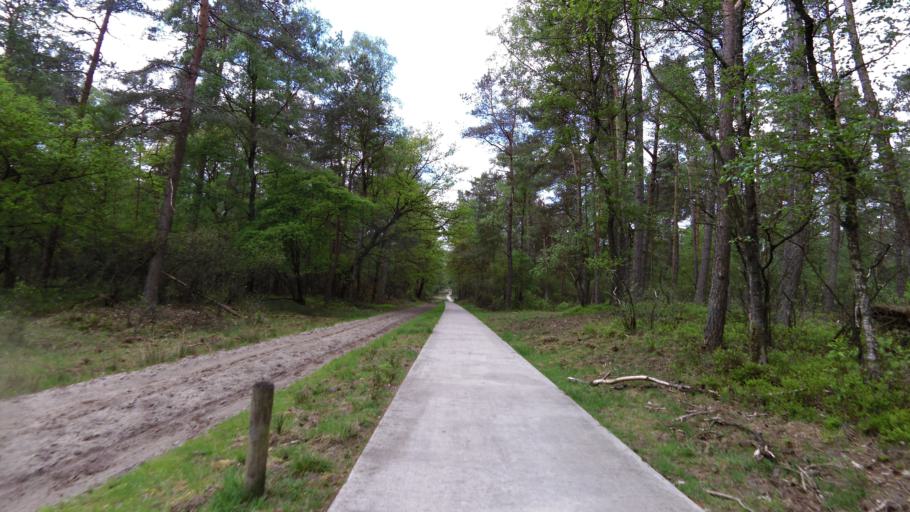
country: NL
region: Gelderland
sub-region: Gemeente Brummen
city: Eerbeek
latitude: 52.0694
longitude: 6.0632
